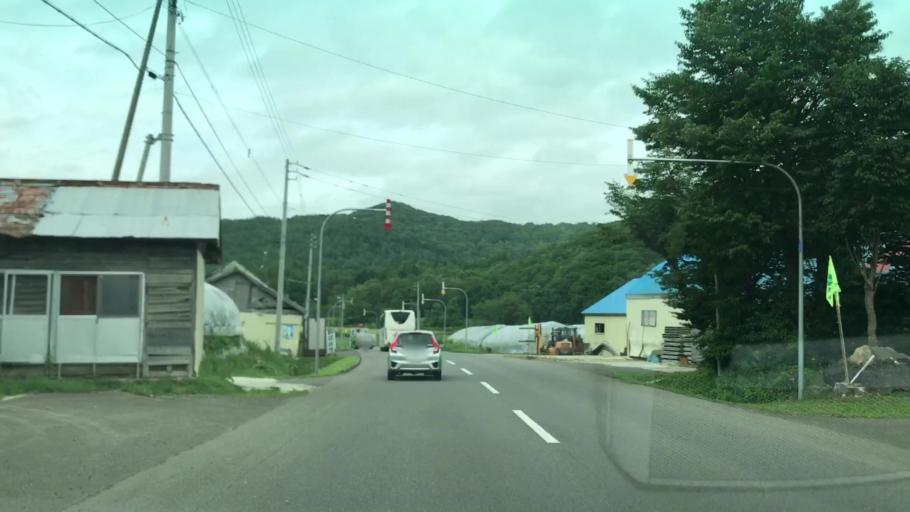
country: JP
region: Hokkaido
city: Niseko Town
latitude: 42.9484
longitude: 140.8322
